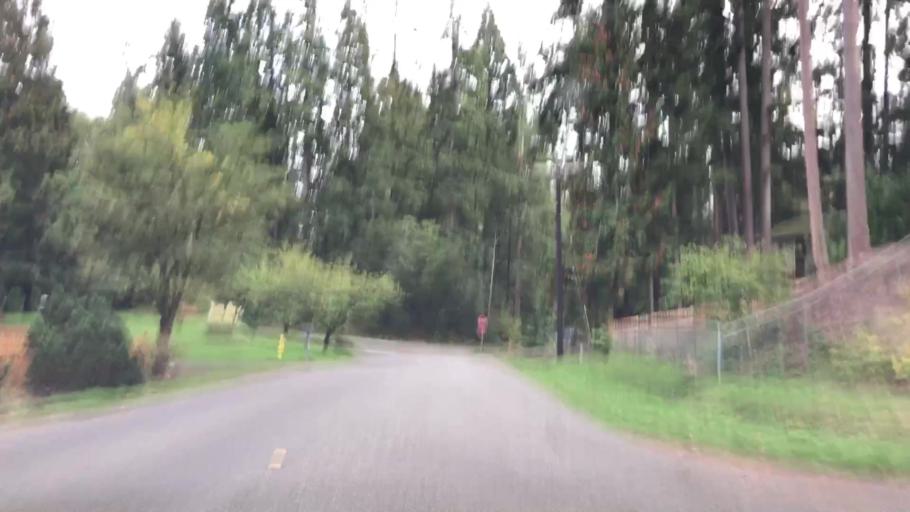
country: US
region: Washington
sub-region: King County
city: Cottage Lake
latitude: 47.7429
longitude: -122.0992
